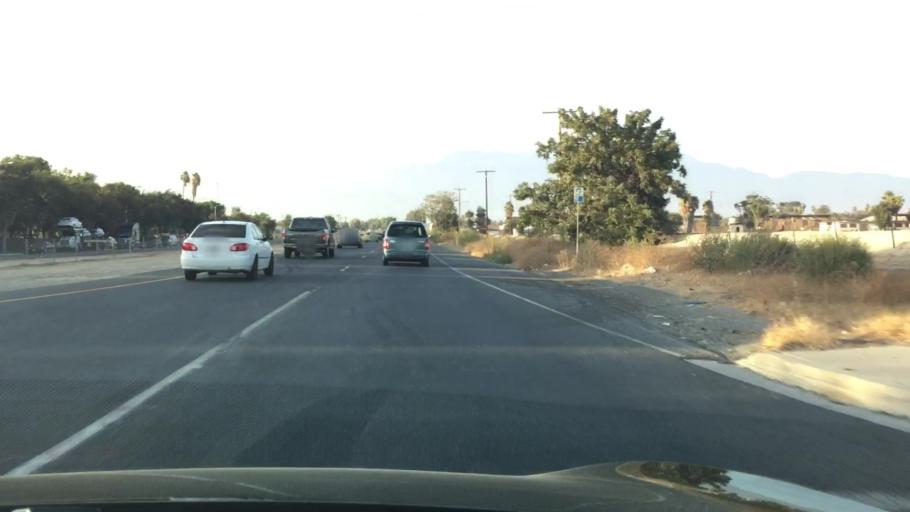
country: US
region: California
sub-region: San Bernardino County
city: Chino
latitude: 34.0122
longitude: -117.6506
